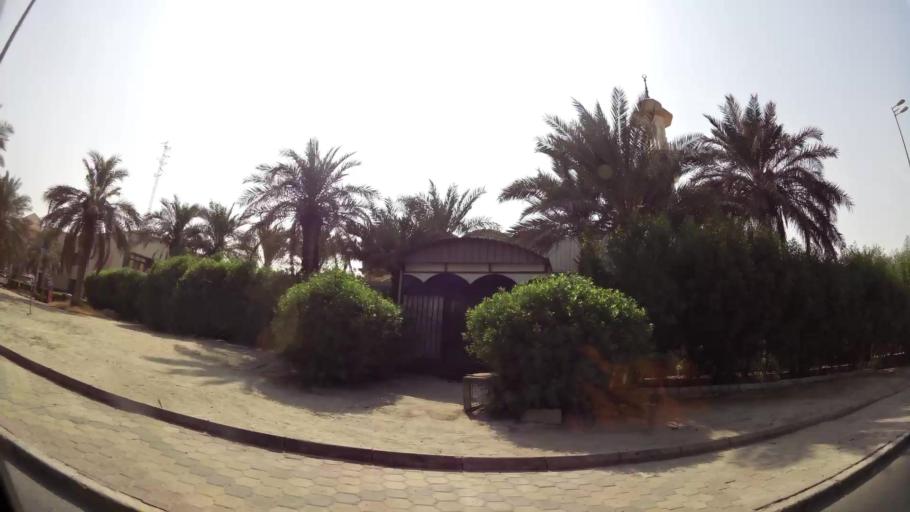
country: KW
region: Al Asimah
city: Ad Dasmah
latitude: 29.3570
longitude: 48.0212
